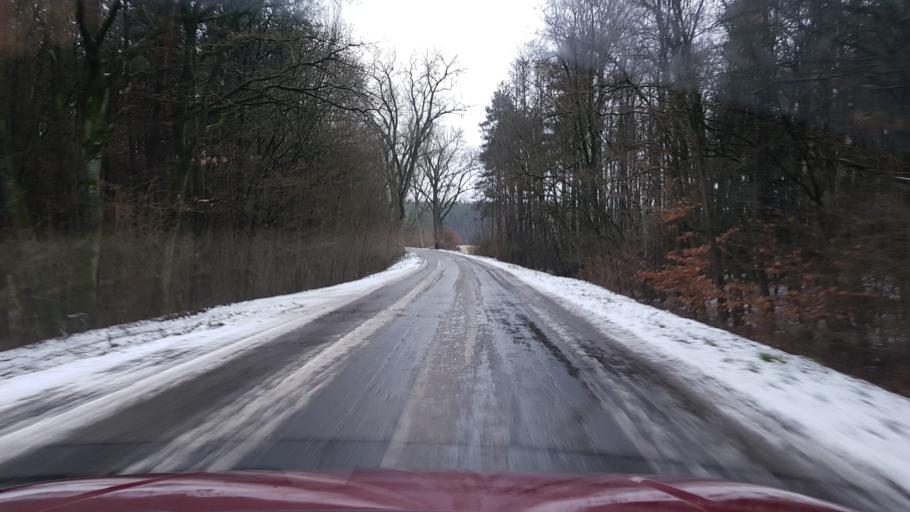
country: PL
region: West Pomeranian Voivodeship
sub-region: Powiat goleniowski
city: Nowogard
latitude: 53.6394
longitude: 15.1216
